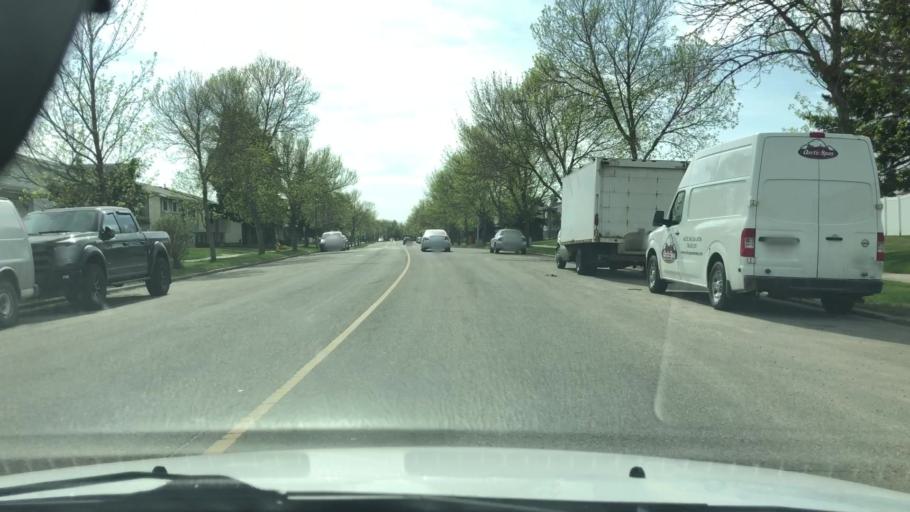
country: CA
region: Alberta
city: Edmonton
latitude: 53.6020
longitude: -113.5192
